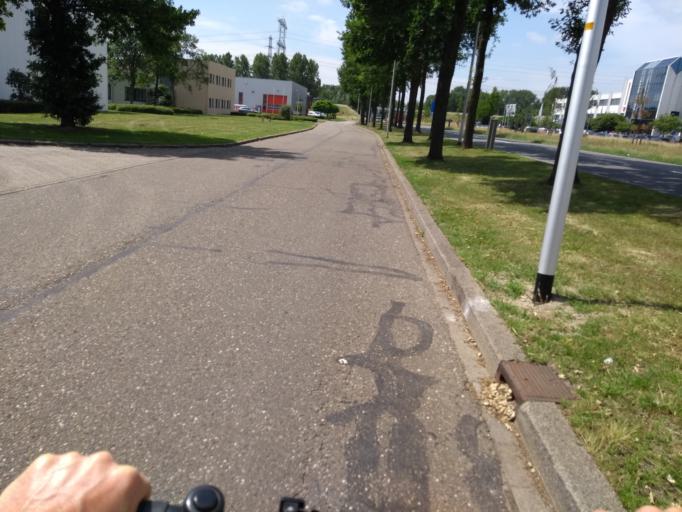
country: NL
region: Overijssel
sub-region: Gemeente Wierden
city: Wierden
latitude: 52.3690
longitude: 6.6140
